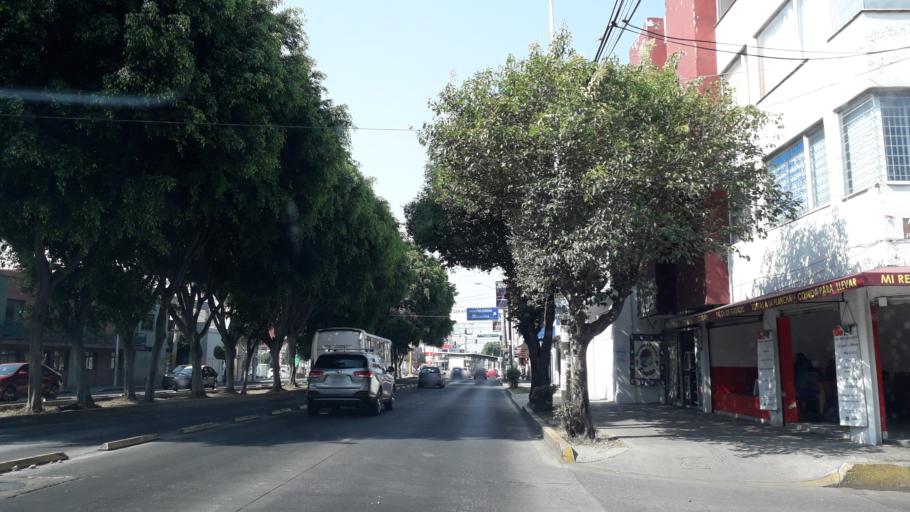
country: MX
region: Puebla
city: Puebla
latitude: 19.0375
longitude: -98.2126
